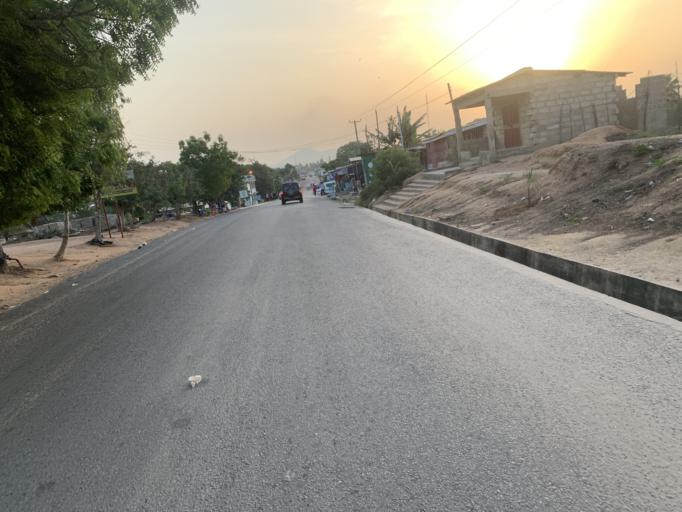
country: GH
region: Central
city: Winneba
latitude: 5.3531
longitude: -0.6170
